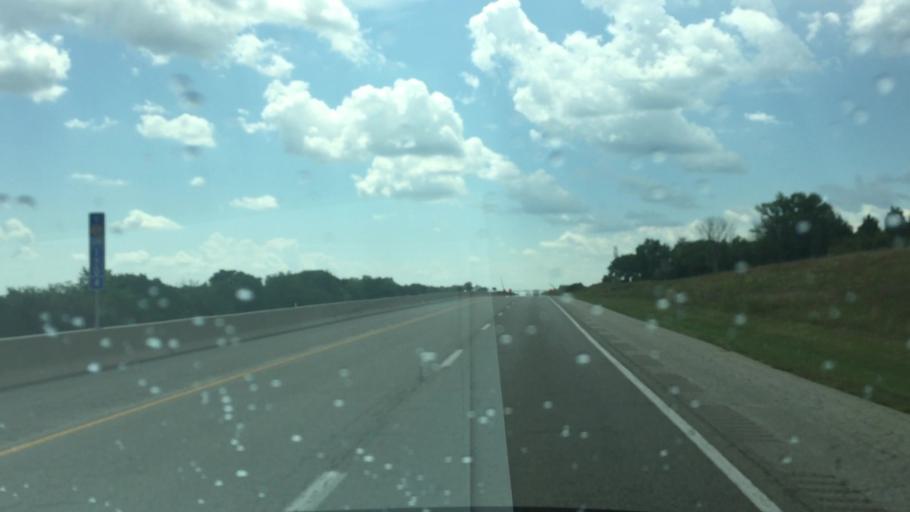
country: US
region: Kansas
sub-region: Shawnee County
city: Auburn
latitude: 38.9222
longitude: -95.7748
